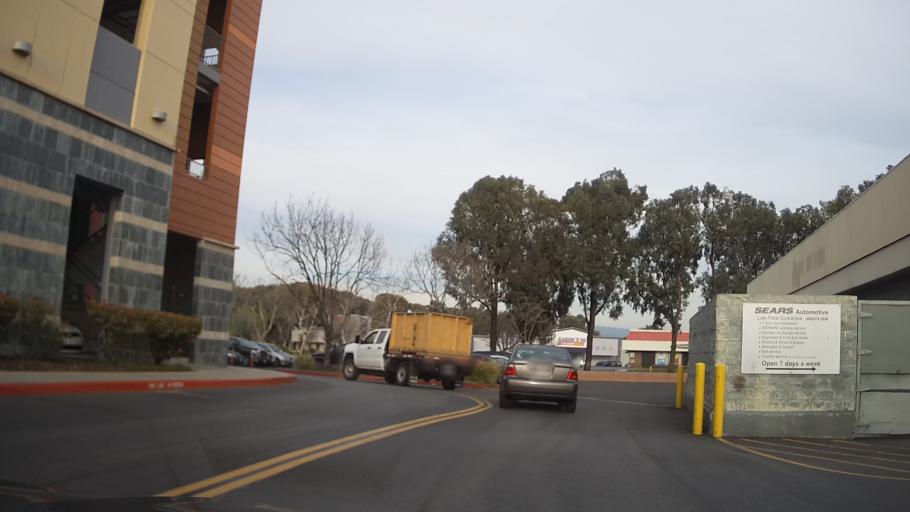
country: US
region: California
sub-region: Santa Clara County
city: Seven Trees
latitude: 37.2511
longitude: -121.8606
